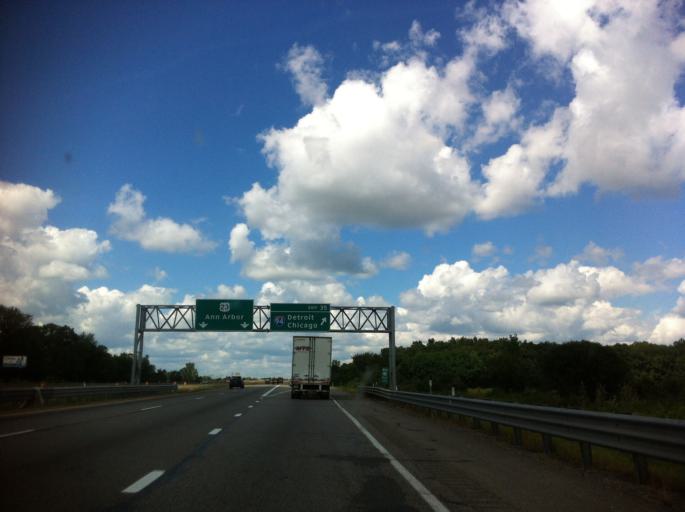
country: US
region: Michigan
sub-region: Washtenaw County
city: Ypsilanti
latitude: 42.2186
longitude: -83.6851
